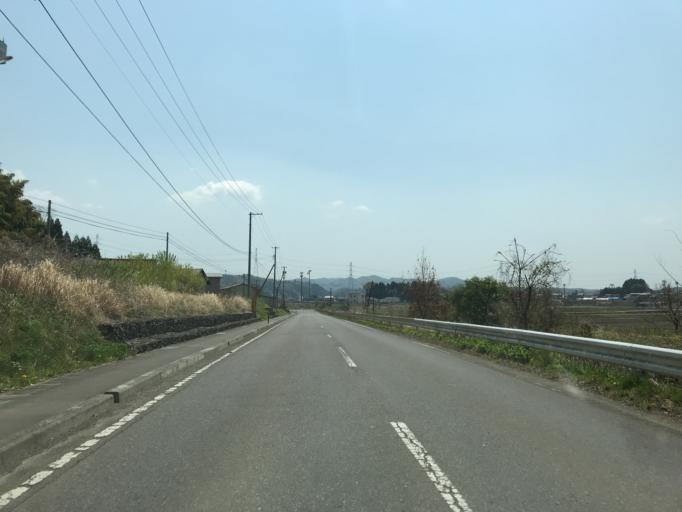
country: JP
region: Fukushima
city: Ishikawa
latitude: 37.0906
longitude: 140.4127
